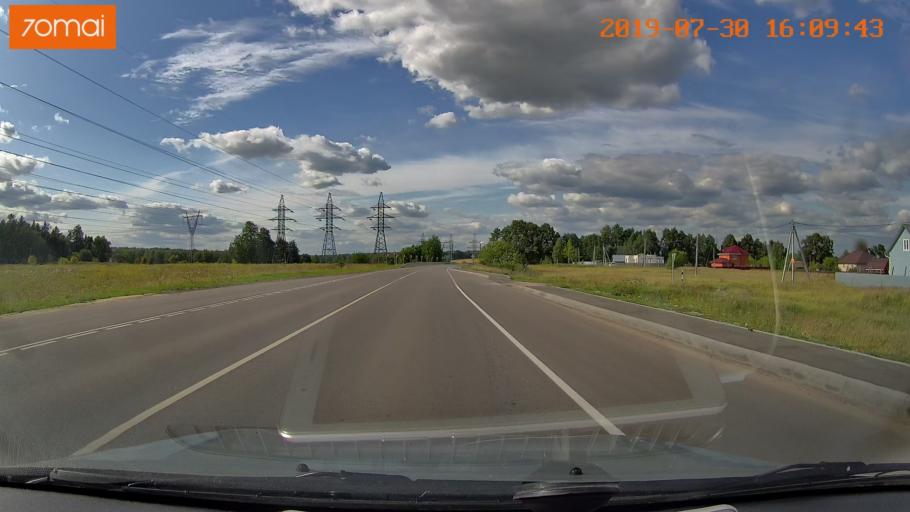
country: RU
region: Moskovskaya
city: Peski
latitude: 55.2555
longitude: 38.7169
